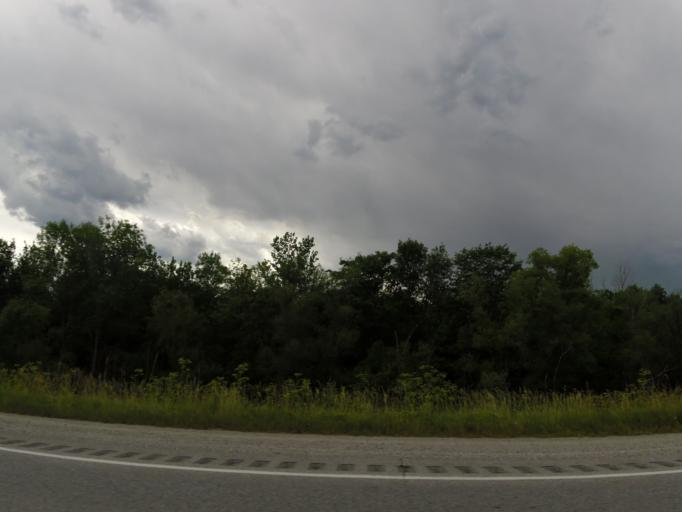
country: US
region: Iowa
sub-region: Johnson County
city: Lone Tree
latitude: 41.4764
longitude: -91.5507
